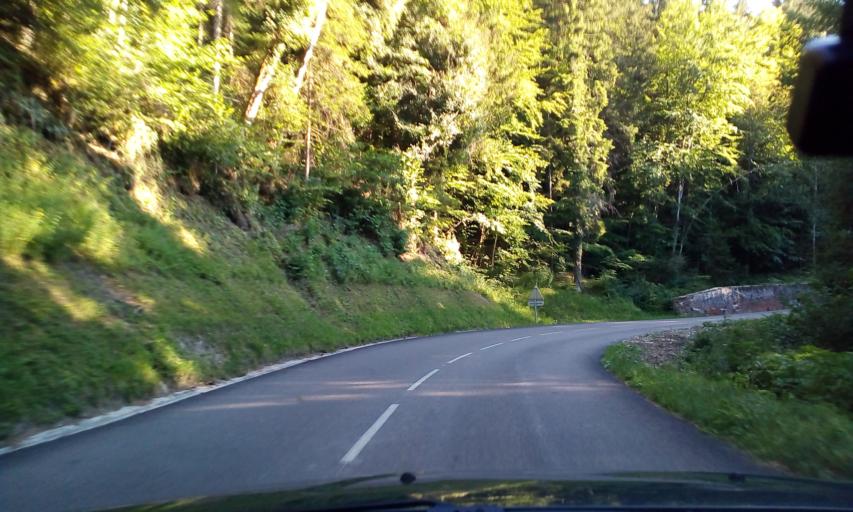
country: FR
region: Rhone-Alpes
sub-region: Departement de l'Isere
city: Meaudre
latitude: 45.0801
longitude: 5.4674
